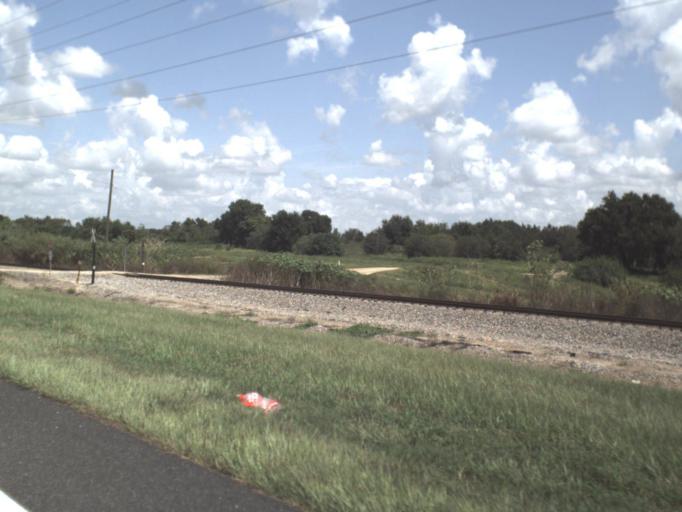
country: US
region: Florida
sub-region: Polk County
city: Bartow
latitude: 27.8454
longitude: -81.8246
